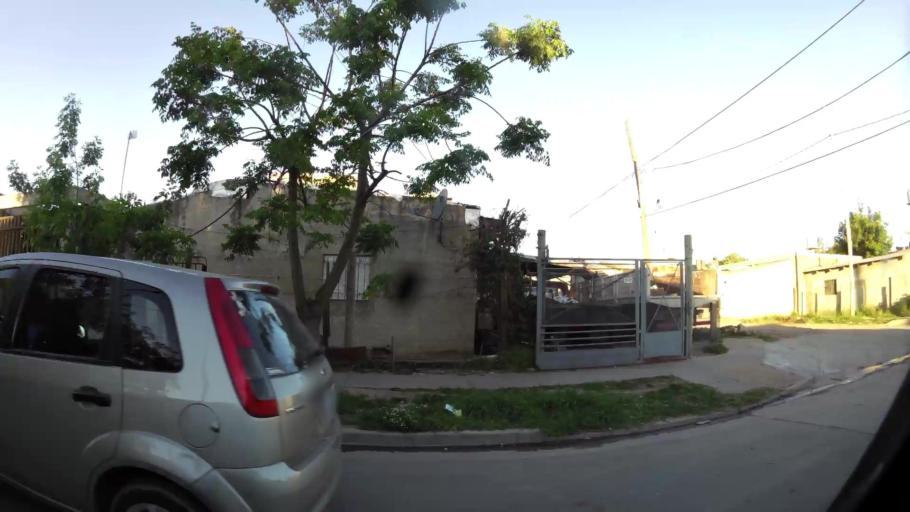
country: AR
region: Buenos Aires
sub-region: Partido de Almirante Brown
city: Adrogue
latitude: -34.7792
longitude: -58.3371
